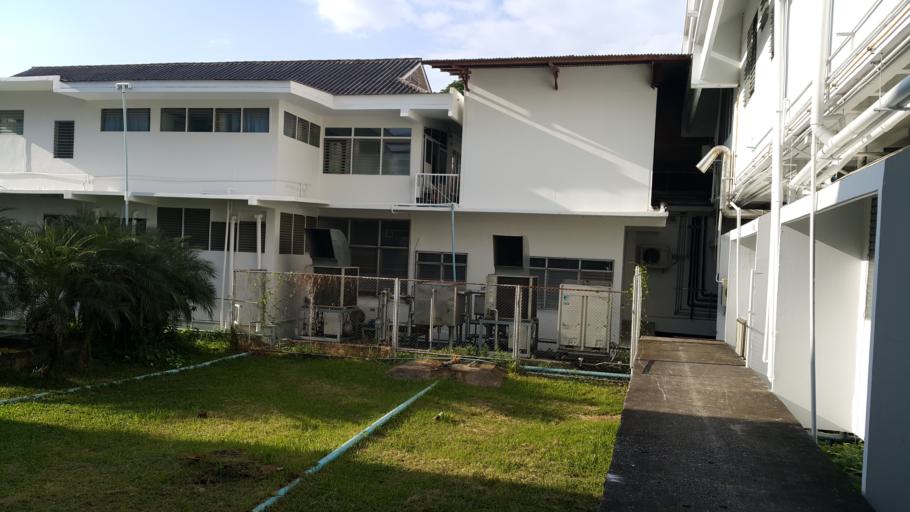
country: TH
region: Chiang Mai
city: Chiang Mai
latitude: 18.7978
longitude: 99.0109
